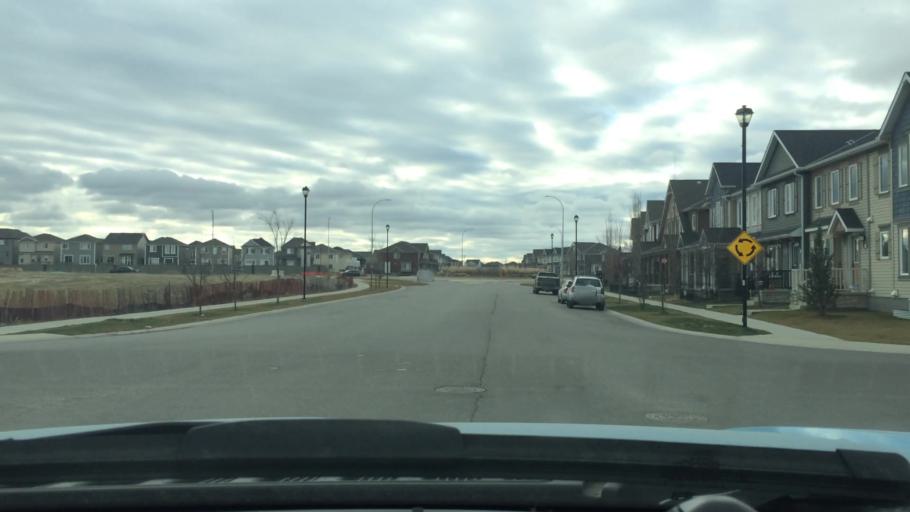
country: CA
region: Alberta
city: Airdrie
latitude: 51.2576
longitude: -114.0324
